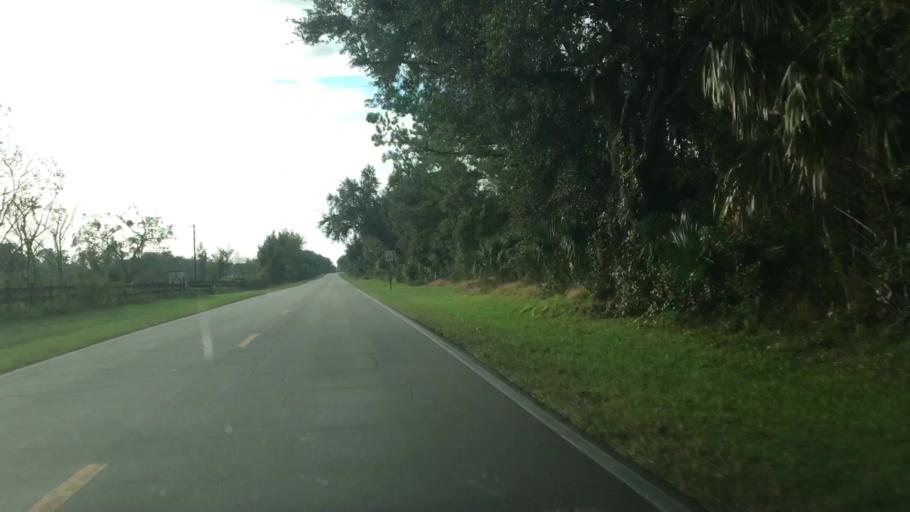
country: US
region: Florida
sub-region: Seminole County
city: Midway
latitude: 28.8387
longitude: -81.1942
